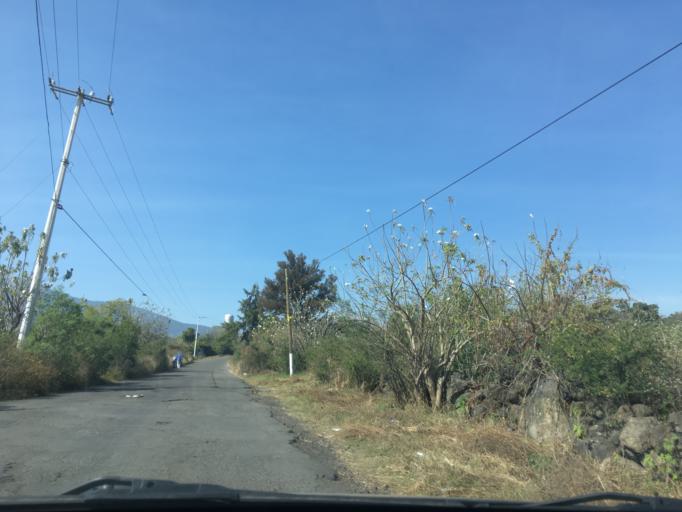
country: MX
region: Michoacan
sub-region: Morelia
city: La Mintzita (Piedra Dura)
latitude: 19.6486
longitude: -101.2914
